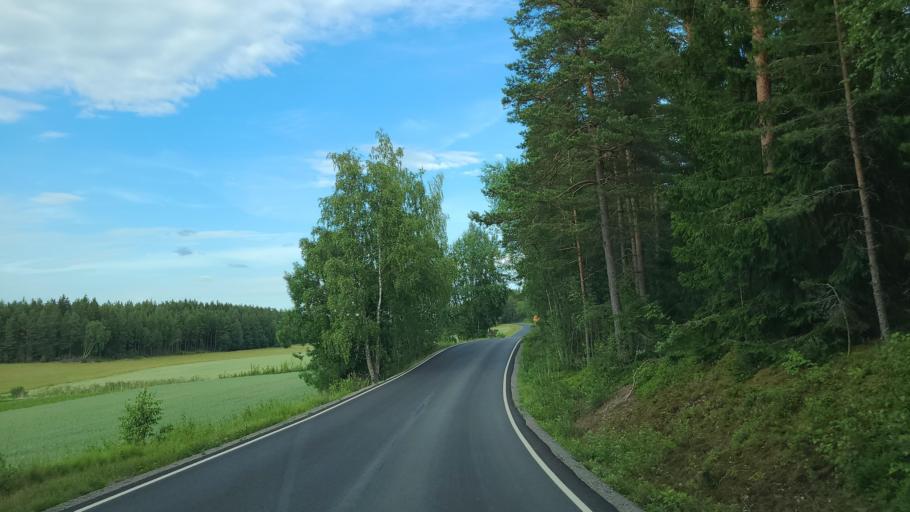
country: FI
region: Varsinais-Suomi
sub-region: Turku
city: Rymaettylae
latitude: 60.3255
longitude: 21.9593
